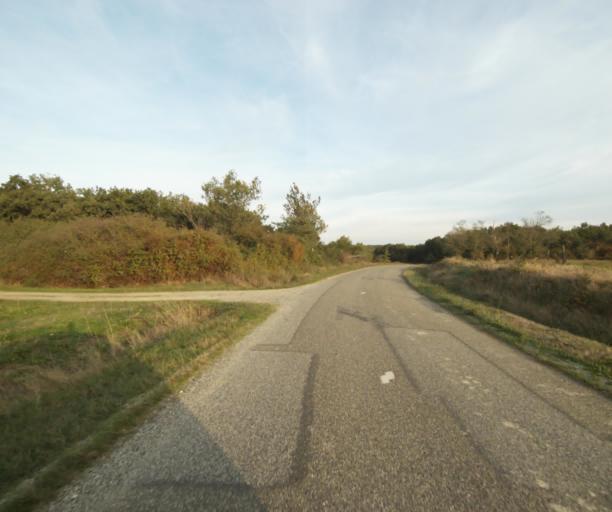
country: FR
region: Midi-Pyrenees
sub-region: Departement du Tarn-et-Garonne
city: Campsas
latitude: 43.8704
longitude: 1.3403
